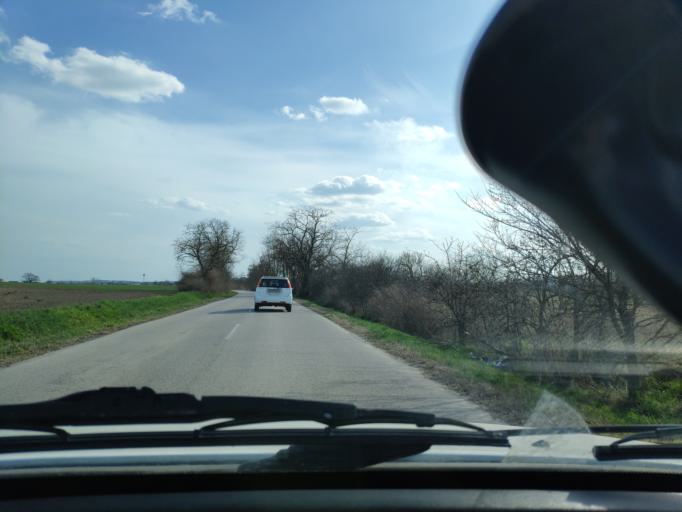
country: HU
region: Fejer
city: Adony
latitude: 47.1280
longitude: 18.8974
